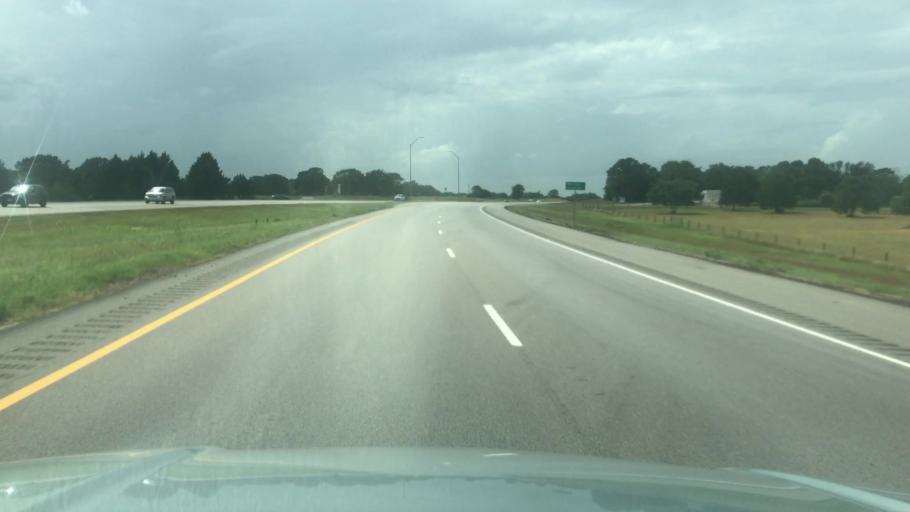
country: US
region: Texas
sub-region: Fayette County
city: La Grange
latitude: 29.9287
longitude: -96.9731
